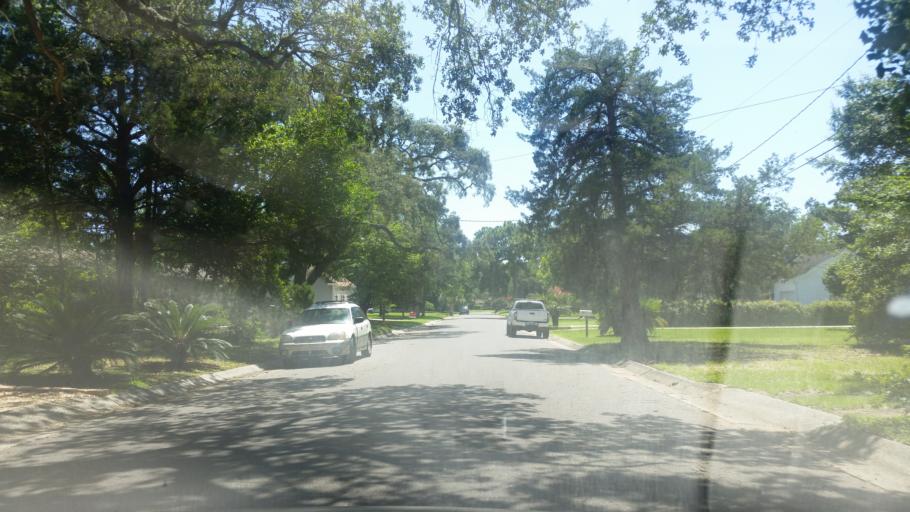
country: US
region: Florida
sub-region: Escambia County
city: East Pensacola Heights
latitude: 30.4379
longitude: -87.1949
